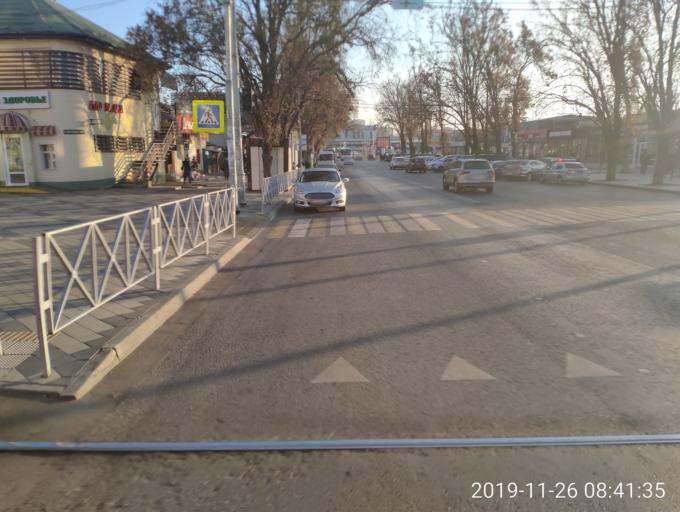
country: RU
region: Krasnodarskiy
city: Krasnodar
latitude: 45.0536
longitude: 38.9835
